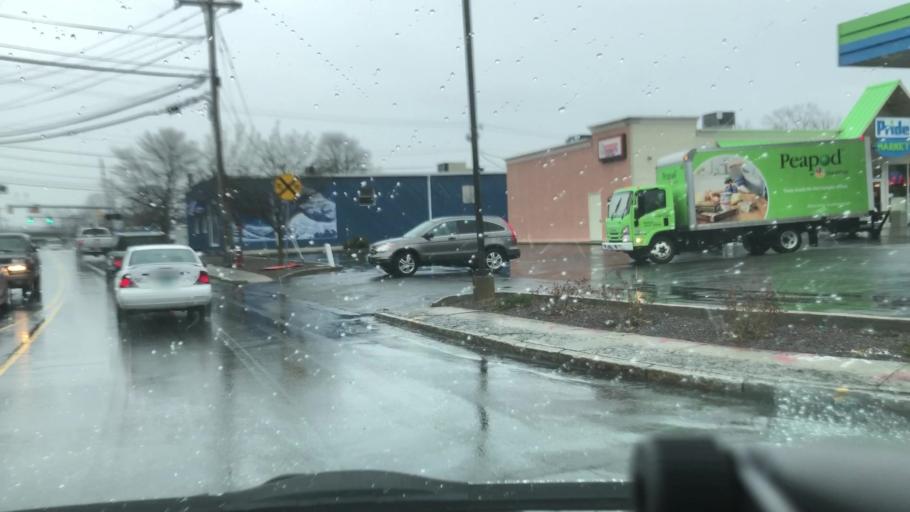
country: US
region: Massachusetts
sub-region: Hampshire County
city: Northampton
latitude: 42.3377
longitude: -72.6372
